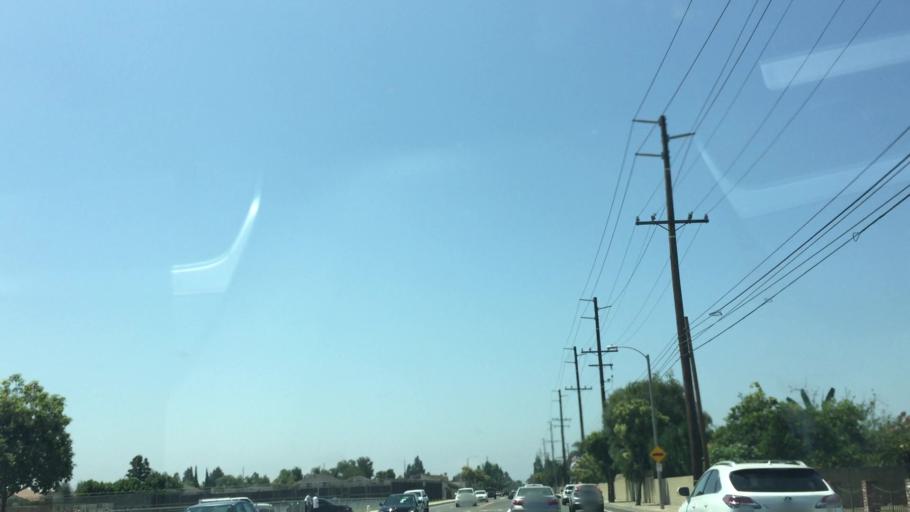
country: US
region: California
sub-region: Orange County
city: Fountain Valley
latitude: 33.7218
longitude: -117.9285
